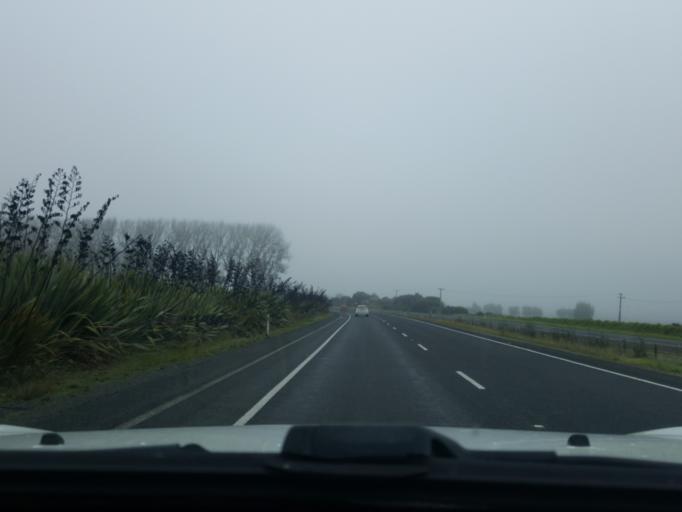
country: NZ
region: Waikato
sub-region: Waikato District
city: Te Kauwhata
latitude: -37.4471
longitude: 175.1521
